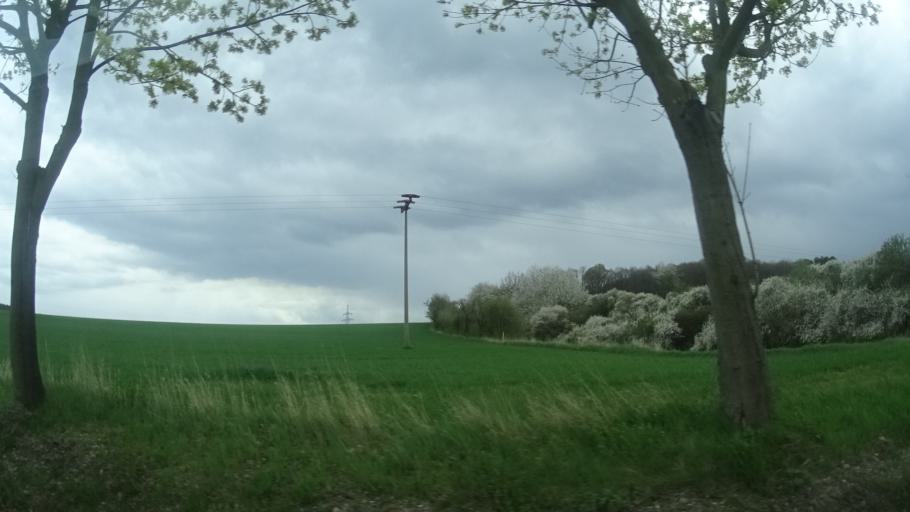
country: DE
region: Thuringia
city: Stadtilm
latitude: 50.7748
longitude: 11.0595
